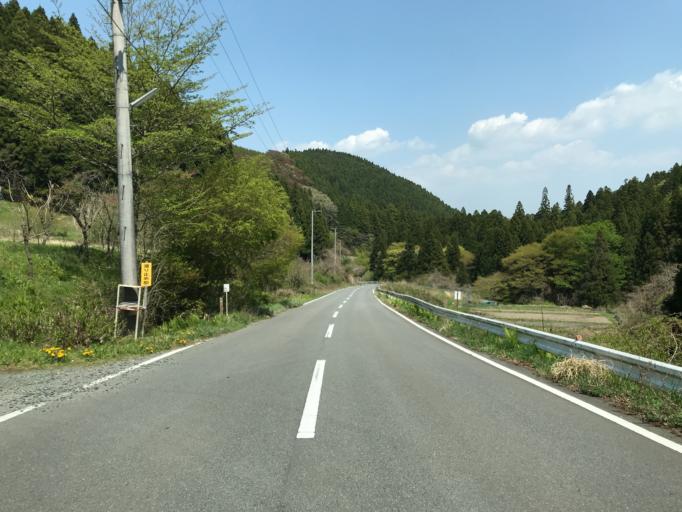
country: JP
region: Ibaraki
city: Kitaibaraki
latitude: 36.9568
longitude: 140.6784
